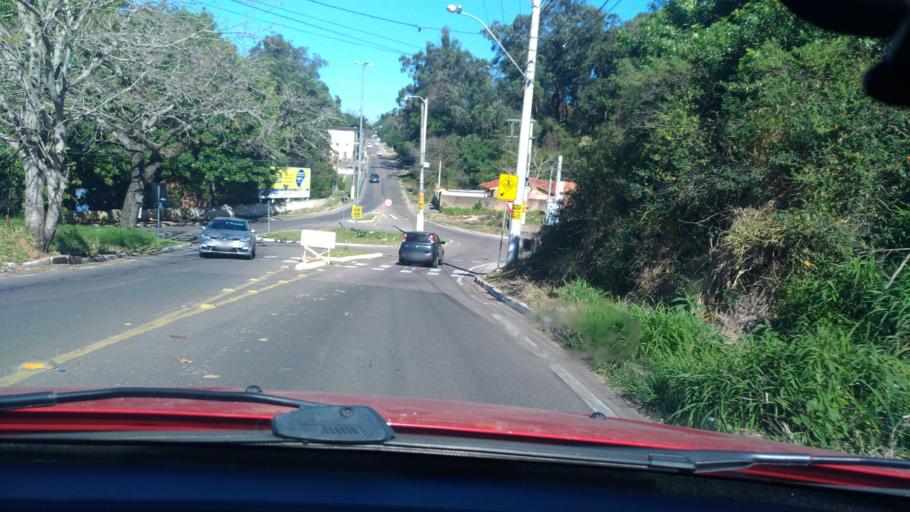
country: BR
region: Rio Grande do Sul
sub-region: Viamao
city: Viamao
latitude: -30.0554
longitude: -51.1054
